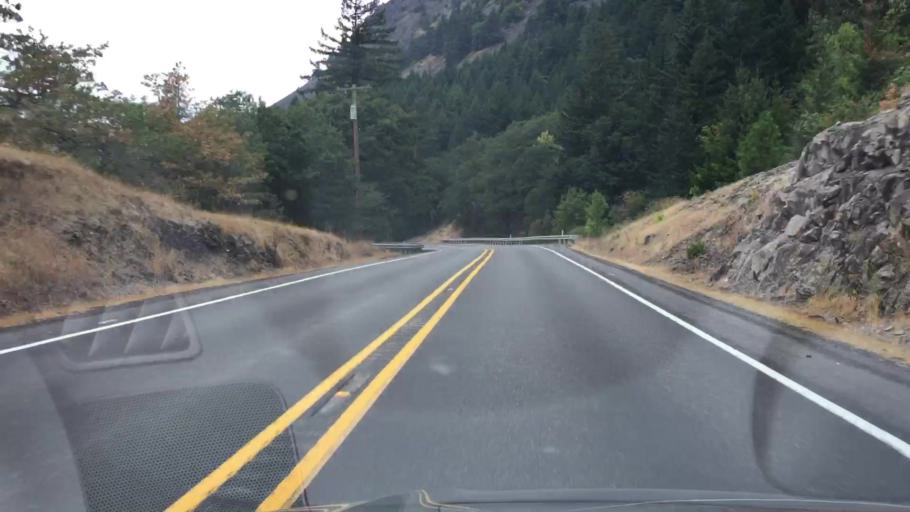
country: US
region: Washington
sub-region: Skamania County
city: Carson
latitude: 45.7020
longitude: -121.7435
